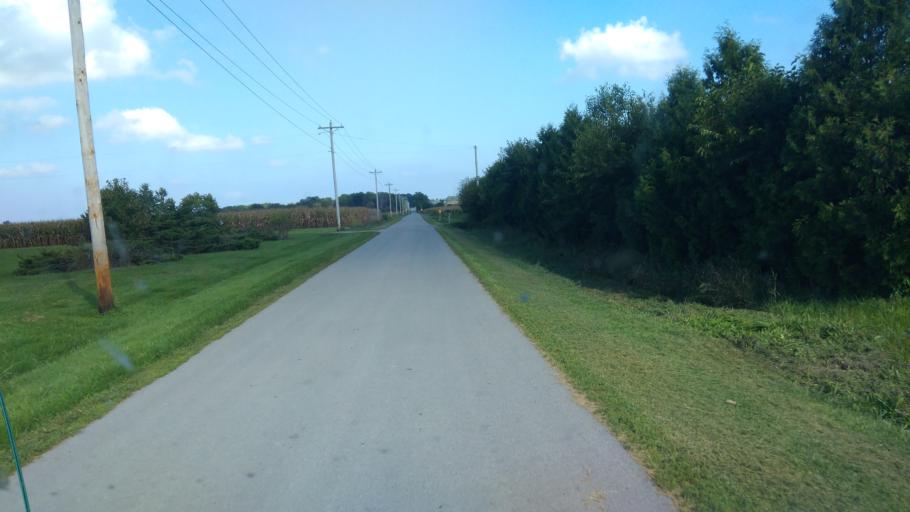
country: US
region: Ohio
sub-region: Hancock County
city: Arlington
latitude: 40.8485
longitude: -83.7140
